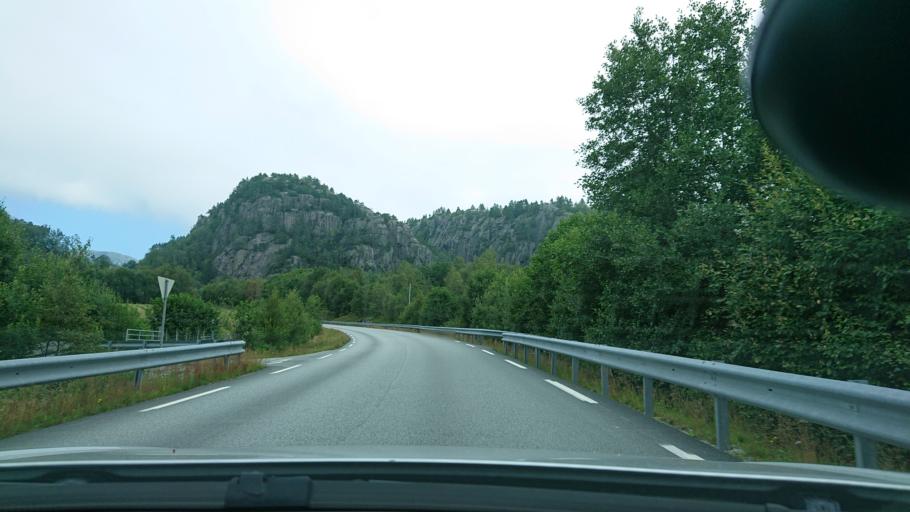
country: NO
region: Rogaland
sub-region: Hjelmeland
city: Hjelmelandsvagen
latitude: 59.2188
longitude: 6.2282
